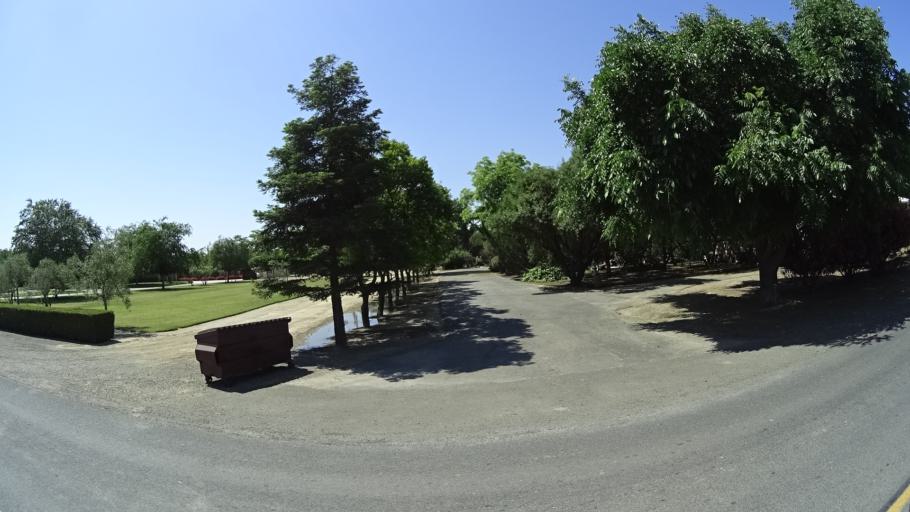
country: US
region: California
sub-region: Kings County
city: Lucerne
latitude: 36.3717
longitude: -119.7080
